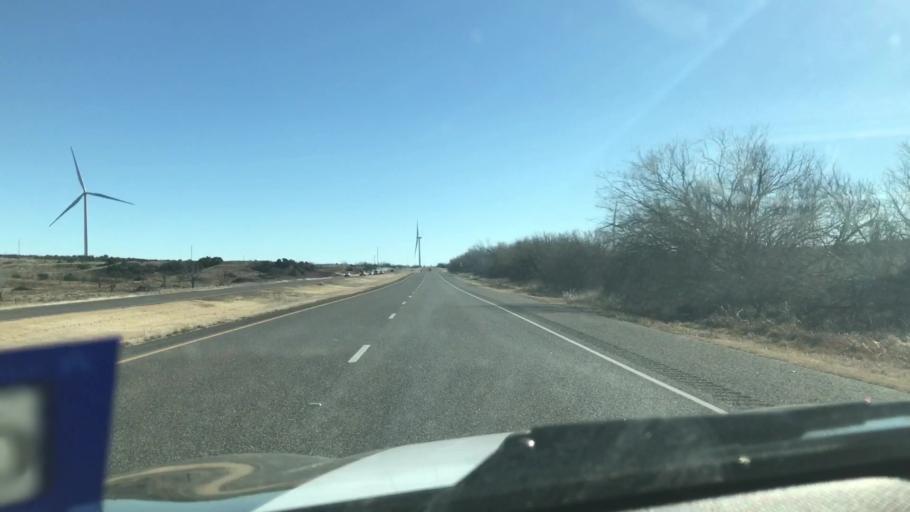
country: US
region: Texas
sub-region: Scurry County
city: Snyder
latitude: 32.8950
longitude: -101.0551
